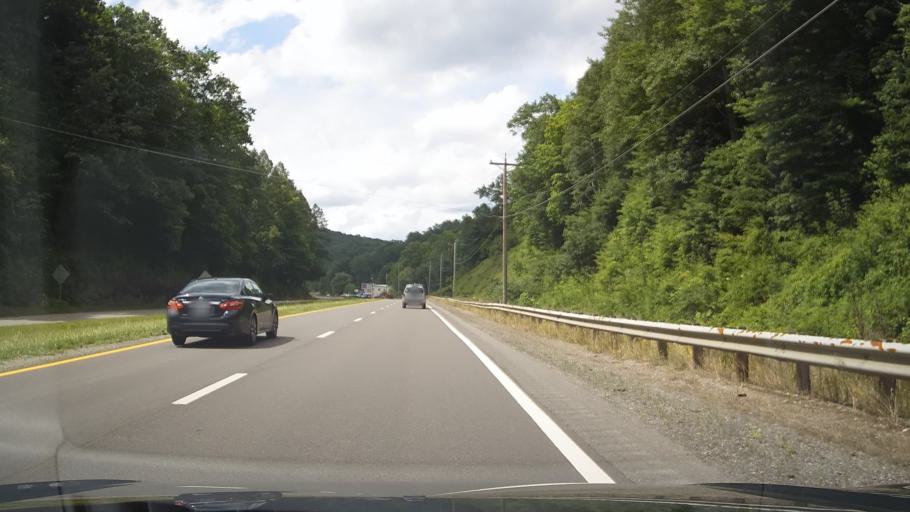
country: US
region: Virginia
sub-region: Wise County
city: Pound
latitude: 37.0524
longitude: -82.5995
